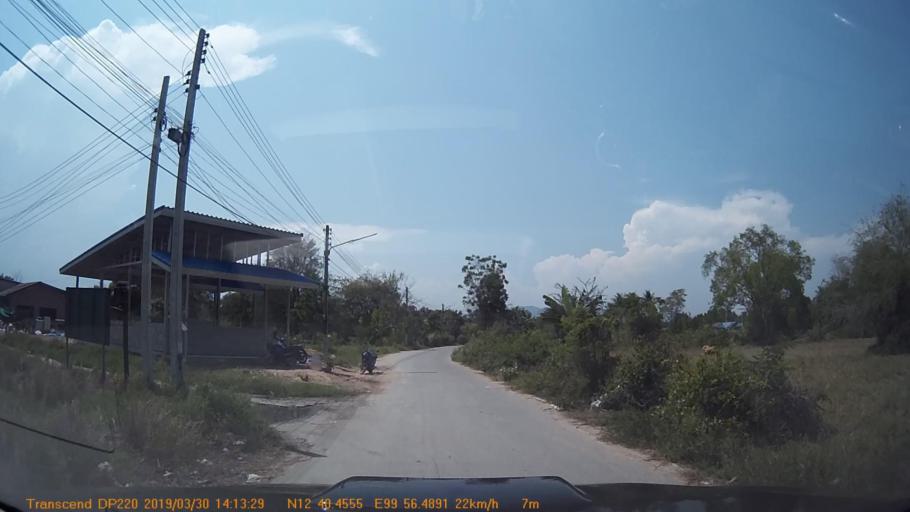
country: TH
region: Prachuap Khiri Khan
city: Hua Hin
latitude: 12.6745
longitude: 99.9414
